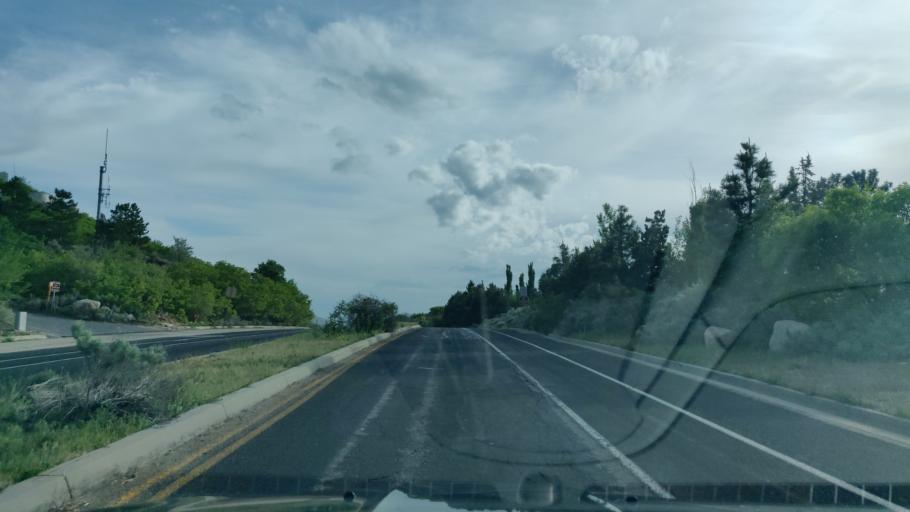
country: US
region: Utah
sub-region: Salt Lake County
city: Granite
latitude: 40.5727
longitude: -111.7991
